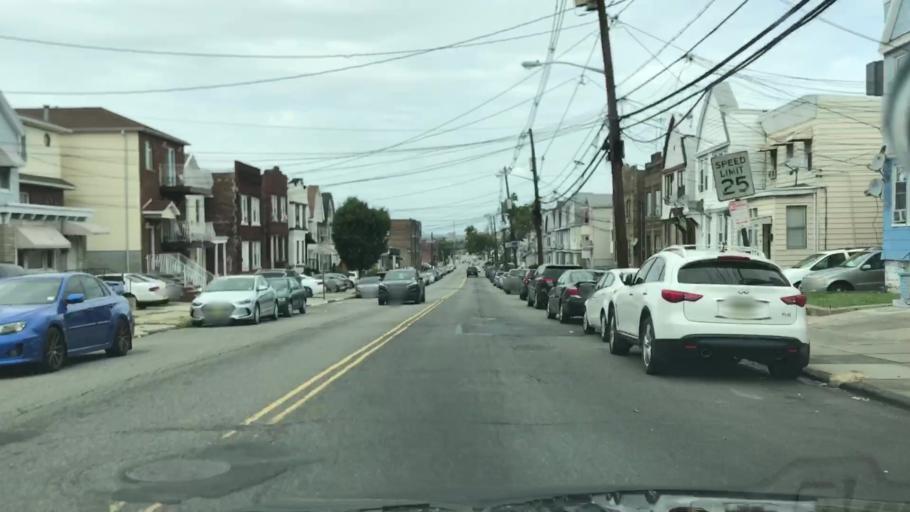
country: US
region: New Jersey
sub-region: Hudson County
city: Jersey City
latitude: 40.7016
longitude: -74.0958
